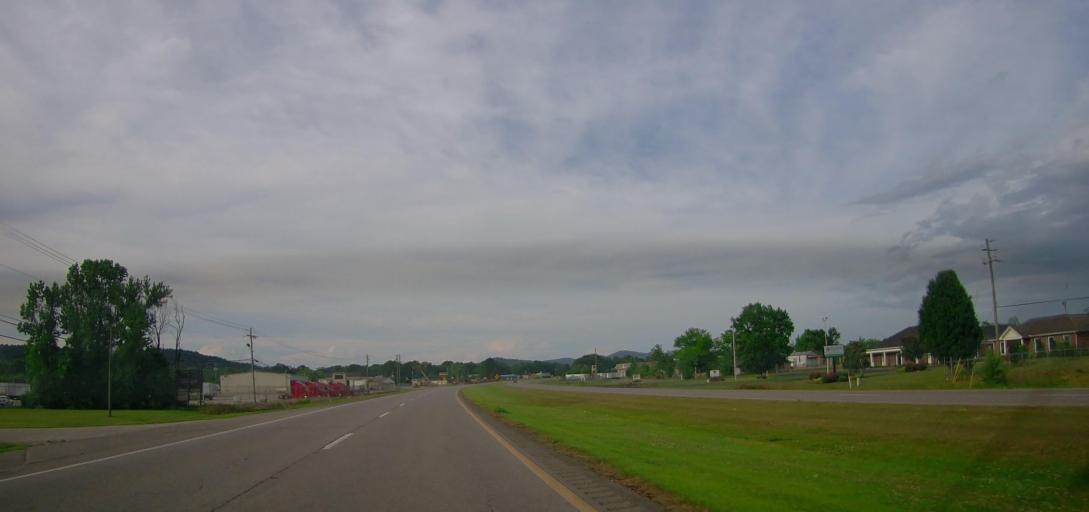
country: US
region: Alabama
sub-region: Calhoun County
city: Oxford
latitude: 33.5912
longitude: -85.8457
